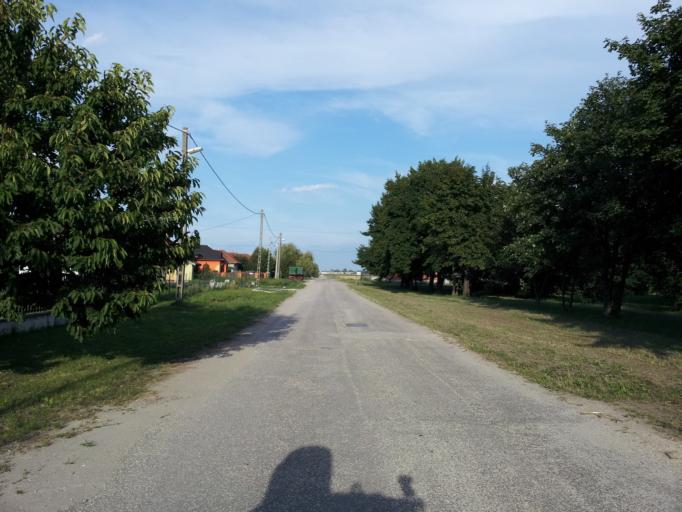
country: HU
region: Pest
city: Kiskunlachaza
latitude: 47.1806
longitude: 19.0093
